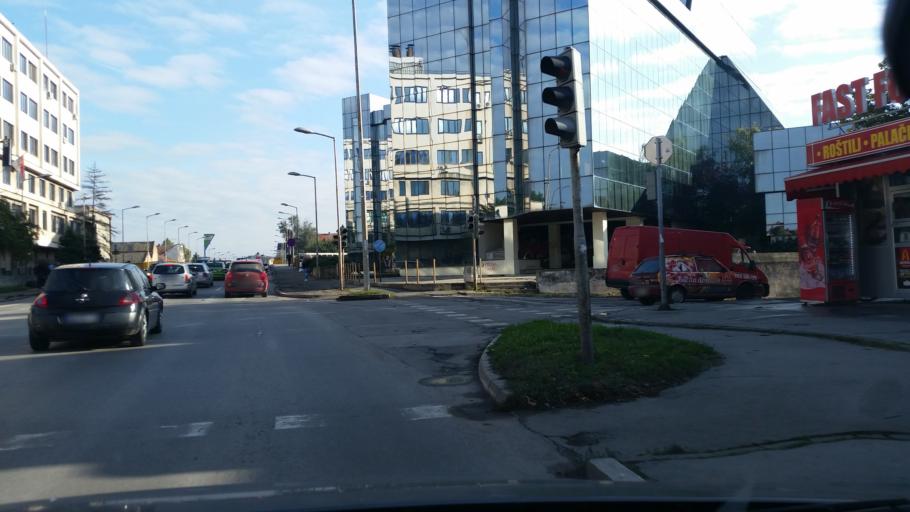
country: RS
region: Autonomna Pokrajina Vojvodina
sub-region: Srednjebanatski Okrug
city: Zrenjanin
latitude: 45.3806
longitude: 20.3972
